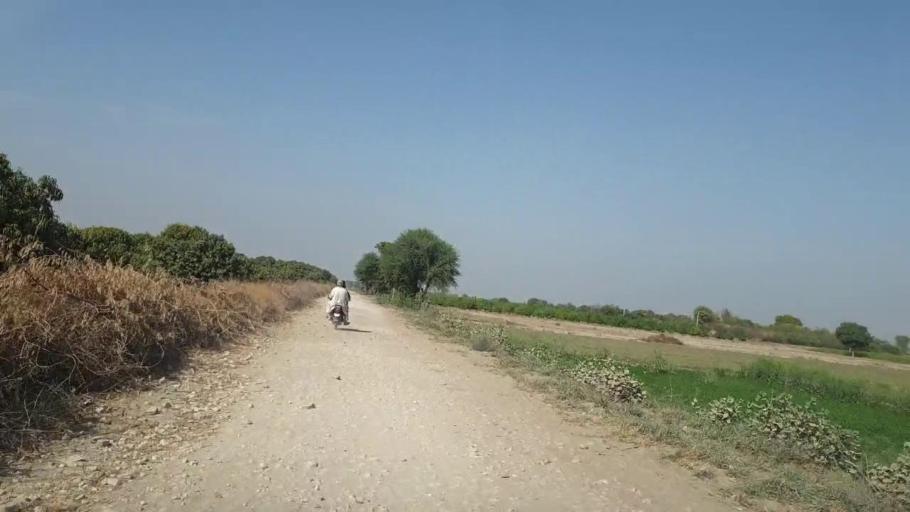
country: PK
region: Sindh
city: Nabisar
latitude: 25.0251
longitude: 69.5244
